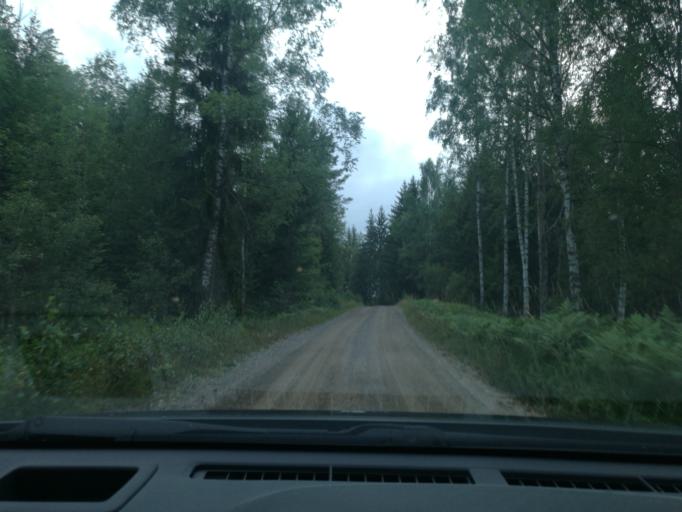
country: SE
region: OEstergoetland
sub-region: Norrkopings Kommun
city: Svartinge
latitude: 58.8118
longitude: 15.9561
